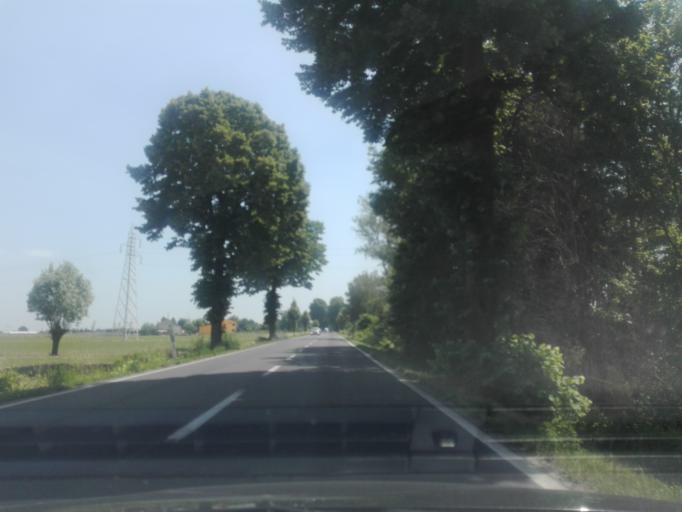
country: IT
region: Veneto
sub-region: Provincia di Rovigo
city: Adria
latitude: 45.0612
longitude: 12.0333
